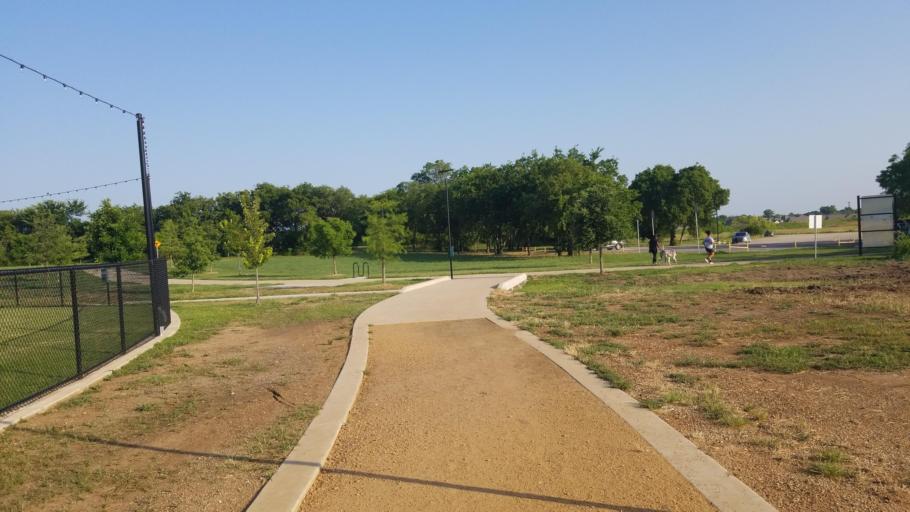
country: US
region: Texas
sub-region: Denton County
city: Denton
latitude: 33.2453
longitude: -97.1463
